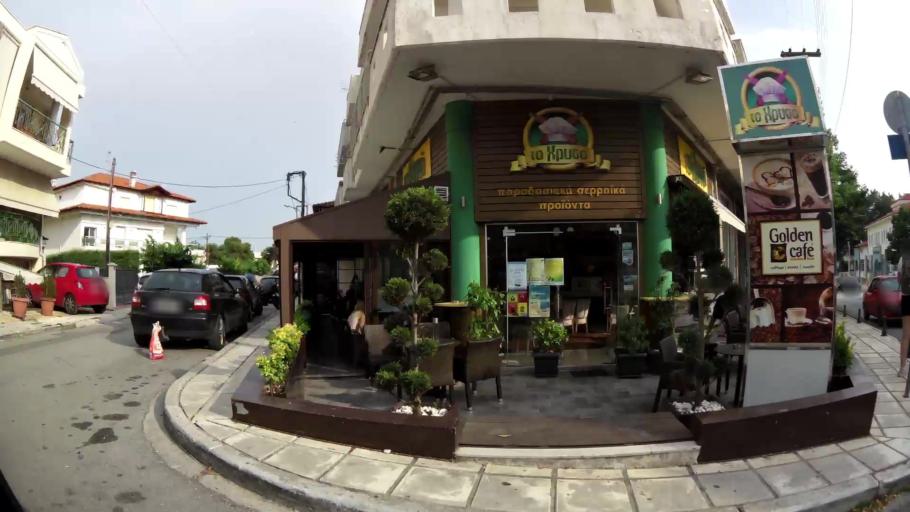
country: GR
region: Central Macedonia
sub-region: Nomos Thessalonikis
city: Oraiokastro
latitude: 40.7276
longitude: 22.9153
